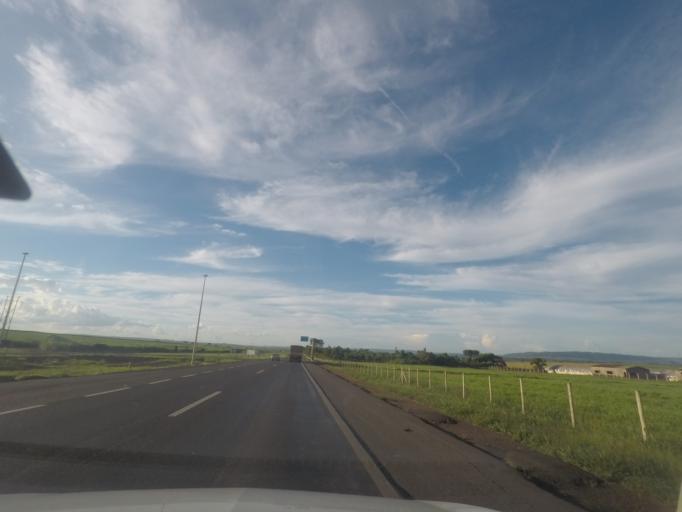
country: BR
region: Goias
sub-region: Itumbiara
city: Itumbiara
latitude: -18.2882
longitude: -49.2393
